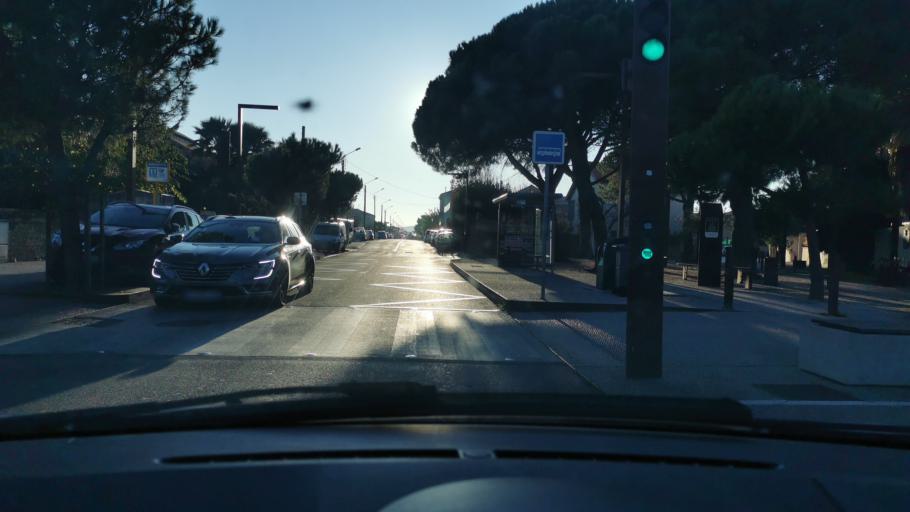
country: FR
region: Languedoc-Roussillon
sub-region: Departement de l'Herault
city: Frontignan
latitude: 43.4442
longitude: 3.7502
